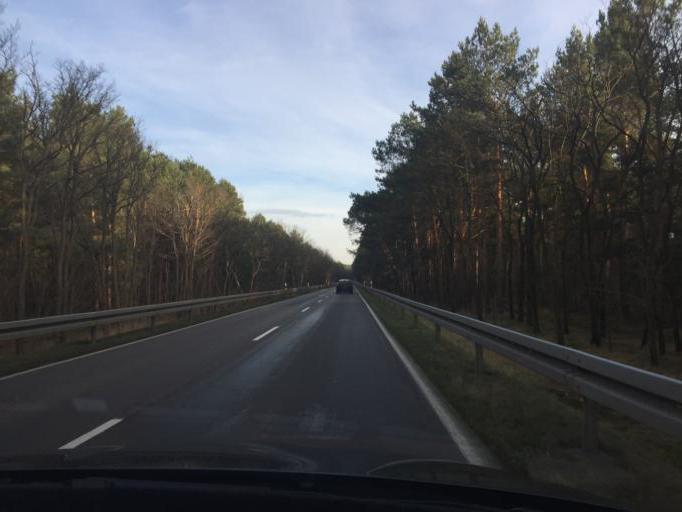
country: DE
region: Brandenburg
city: Heinersbruck
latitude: 51.7268
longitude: 14.5065
